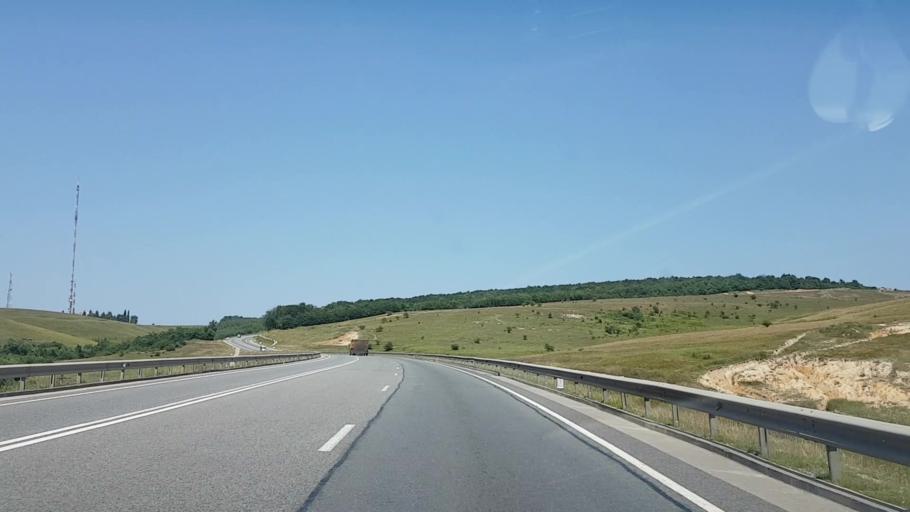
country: RO
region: Cluj
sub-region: Comuna Feleacu
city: Feleacu
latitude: 46.7009
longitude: 23.6406
